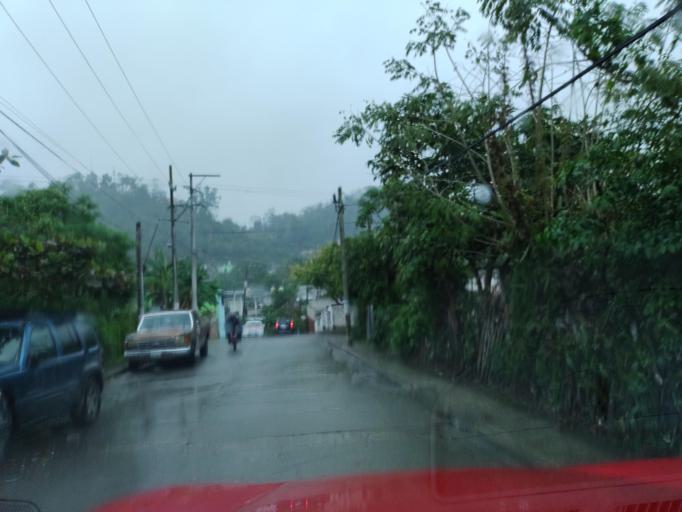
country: MX
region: Veracruz
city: Papantla de Olarte
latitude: 20.4365
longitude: -97.3376
